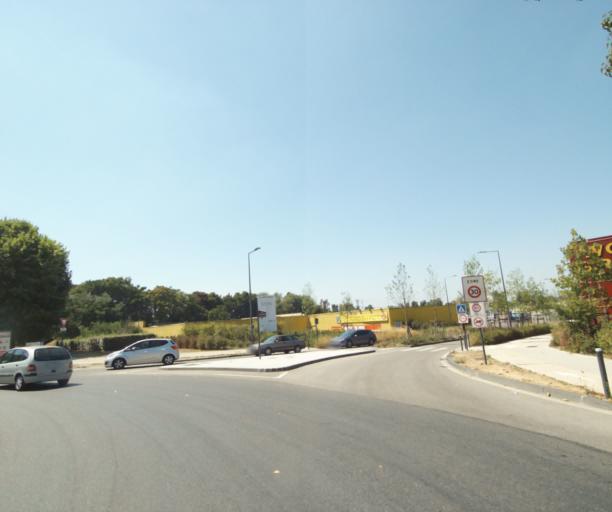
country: FR
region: Ile-de-France
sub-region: Departement de Seine-et-Marne
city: Saint-Thibault-des-Vignes
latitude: 48.8675
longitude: 2.6791
